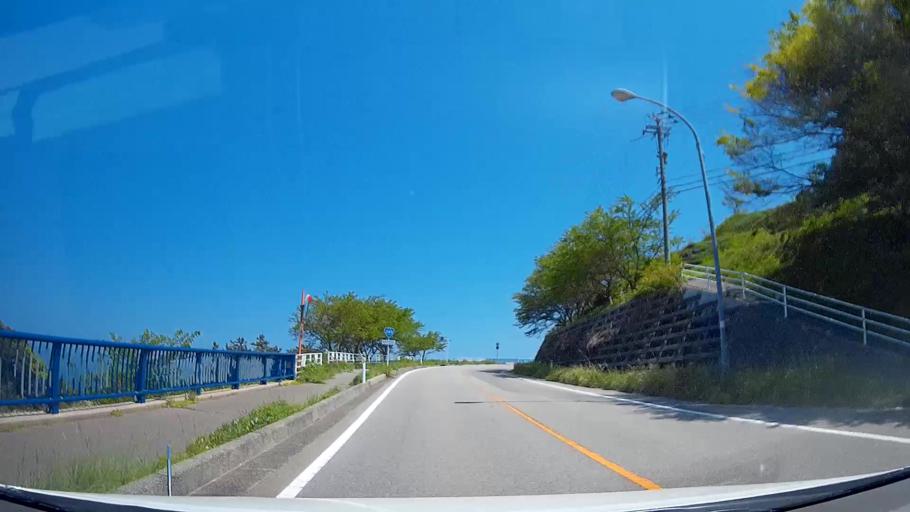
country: JP
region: Ishikawa
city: Nanao
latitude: 37.4155
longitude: 136.9795
